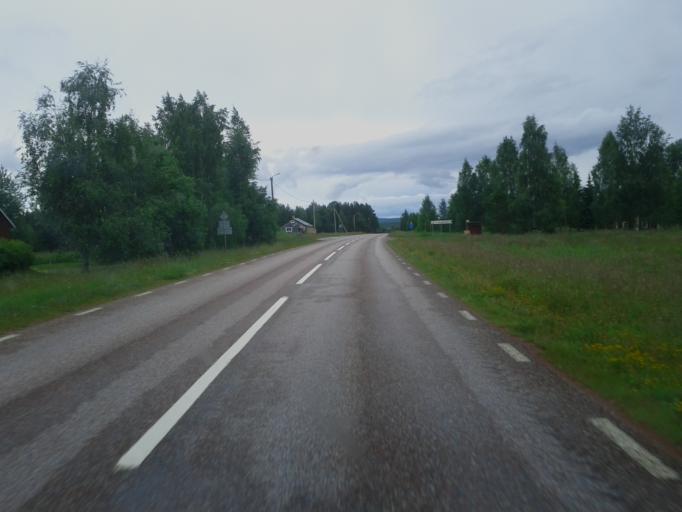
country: NO
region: Hedmark
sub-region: Trysil
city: Innbygda
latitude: 61.7314
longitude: 12.9874
